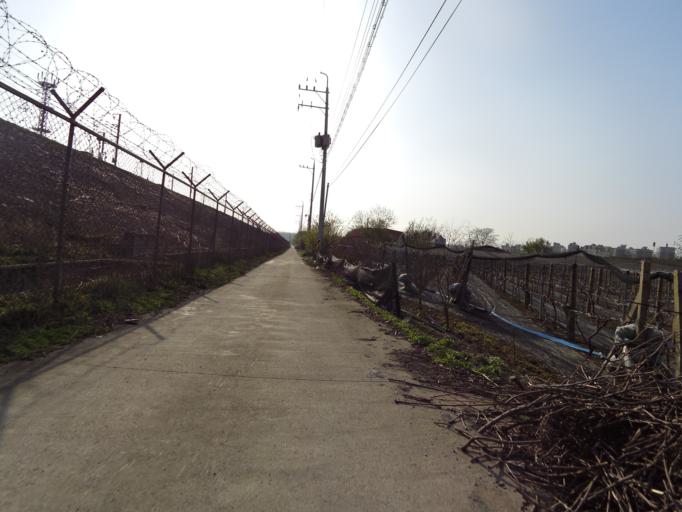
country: KR
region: Gyeongsangbuk-do
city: Gyeongsan-si
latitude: 35.8549
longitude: 128.7043
